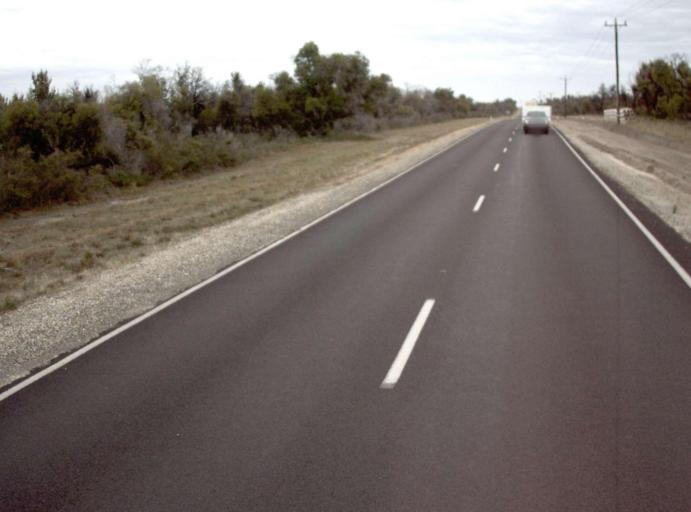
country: AU
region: Victoria
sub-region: East Gippsland
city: Bairnsdale
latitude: -38.1024
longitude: 147.4983
